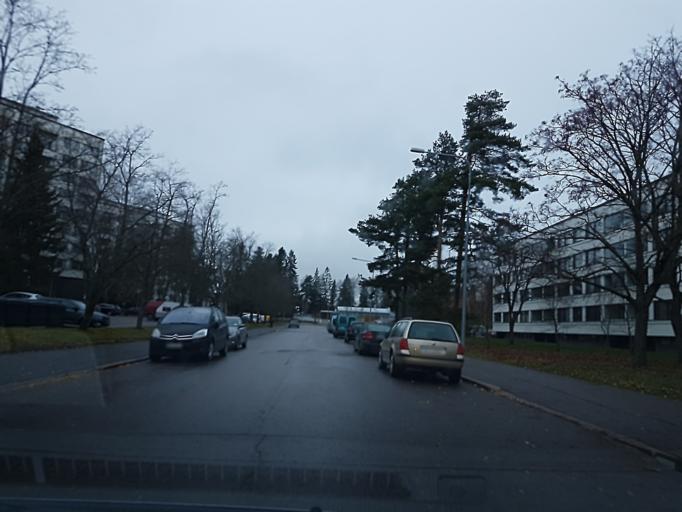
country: FI
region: Uusimaa
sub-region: Helsinki
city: Vantaa
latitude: 60.2334
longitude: 25.0883
